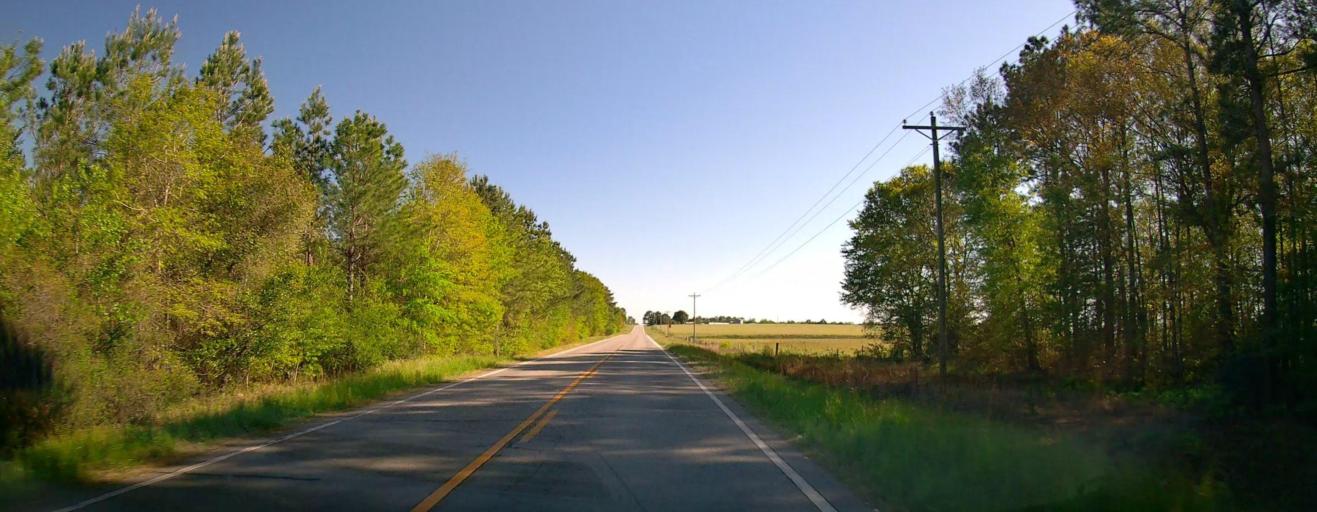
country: US
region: Georgia
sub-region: Wilcox County
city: Rochelle
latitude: 31.8666
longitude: -83.4888
